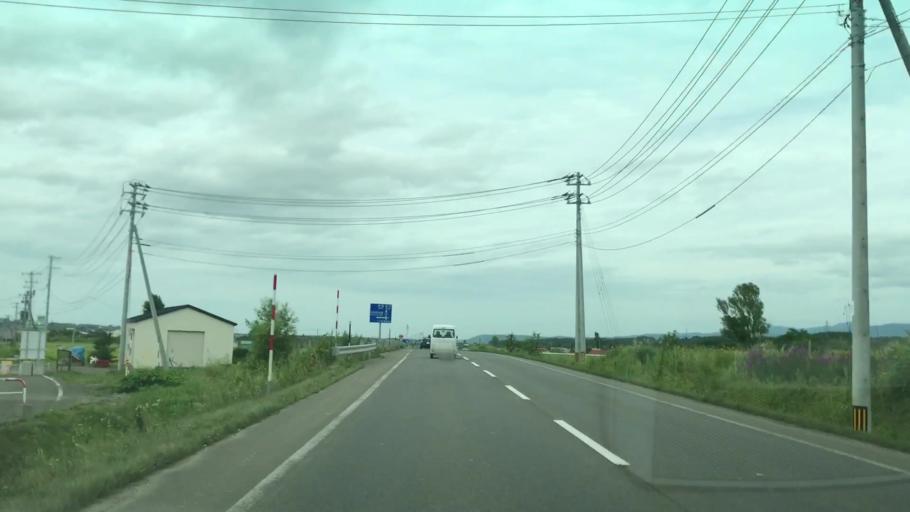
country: JP
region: Hokkaido
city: Iwanai
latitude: 42.9788
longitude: 140.6269
